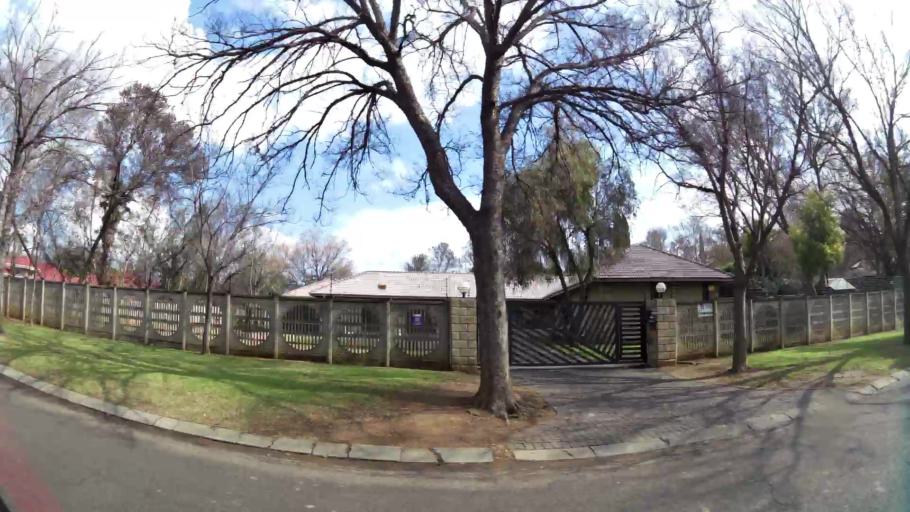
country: ZA
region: Gauteng
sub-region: Sedibeng District Municipality
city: Vanderbijlpark
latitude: -26.7384
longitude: 27.8363
